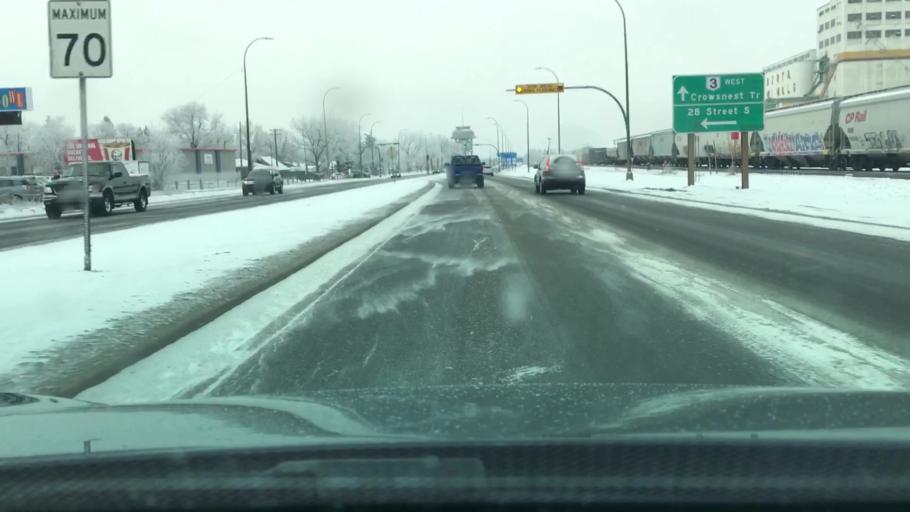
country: CA
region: Alberta
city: Lethbridge
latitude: 49.6982
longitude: -112.7992
